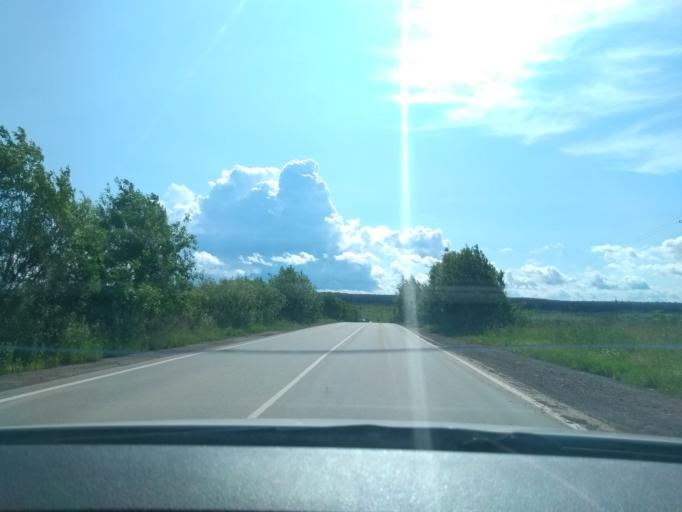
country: RU
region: Perm
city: Bershet'
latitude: 57.8139
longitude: 56.4512
